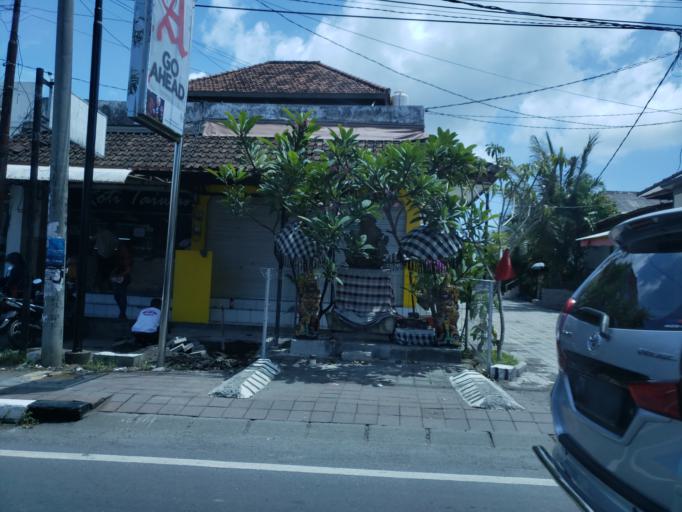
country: ID
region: Bali
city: Jimbaran
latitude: -8.8027
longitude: 115.1600
